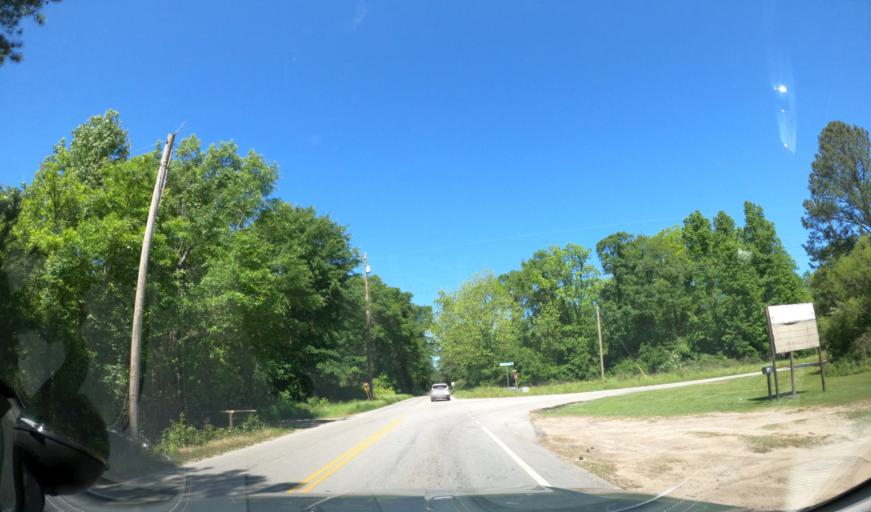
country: US
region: South Carolina
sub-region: Aiken County
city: Clearwater
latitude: 33.4883
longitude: -81.9013
